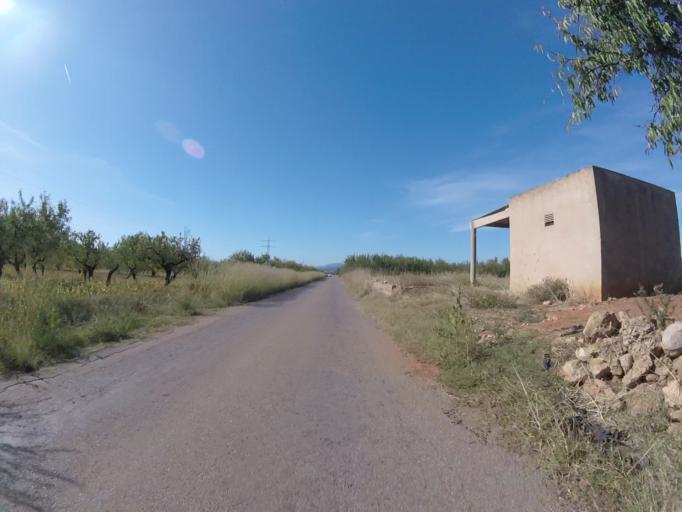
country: ES
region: Valencia
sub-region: Provincia de Castello
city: Torreblanca
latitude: 40.2121
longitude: 0.2122
